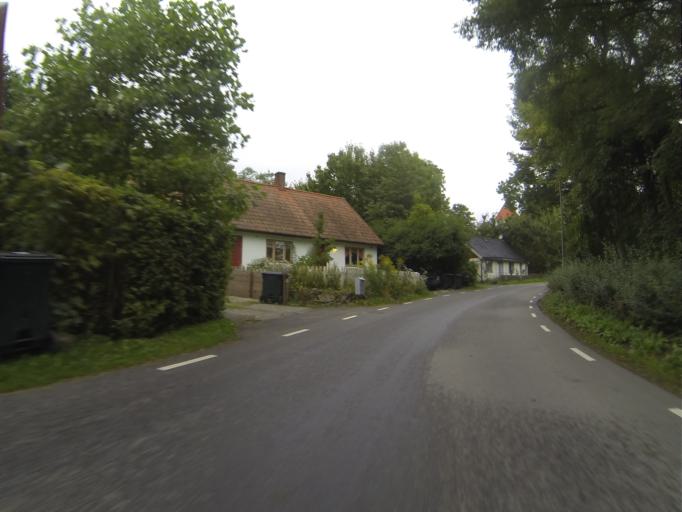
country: SE
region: Skane
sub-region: Lunds Kommun
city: Veberod
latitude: 55.6766
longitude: 13.4216
